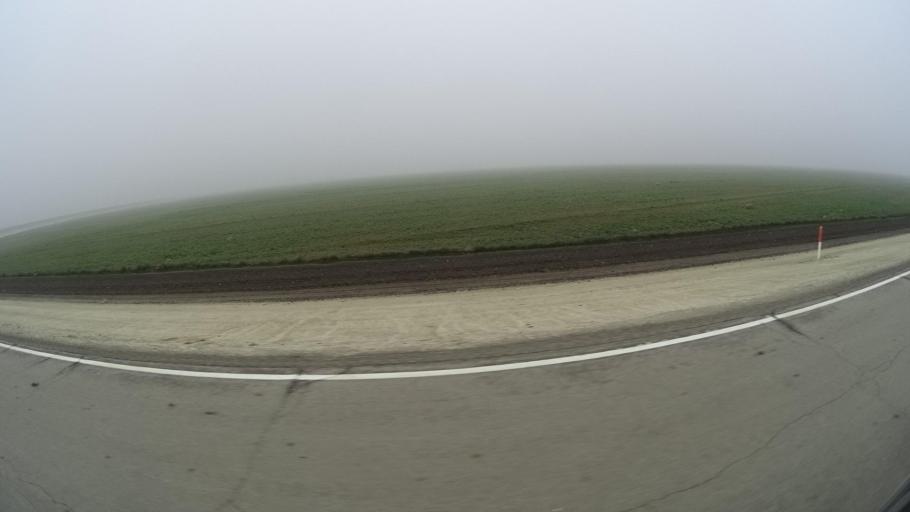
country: US
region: California
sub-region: Kern County
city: Buttonwillow
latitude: 35.4354
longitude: -119.5440
